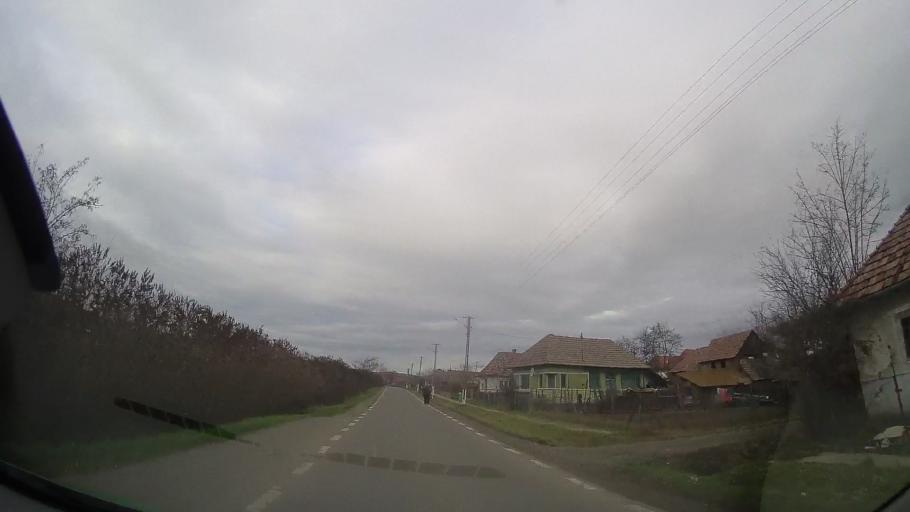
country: RO
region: Mures
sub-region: Comuna Faragau
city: Faragau
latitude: 46.7769
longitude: 24.5566
